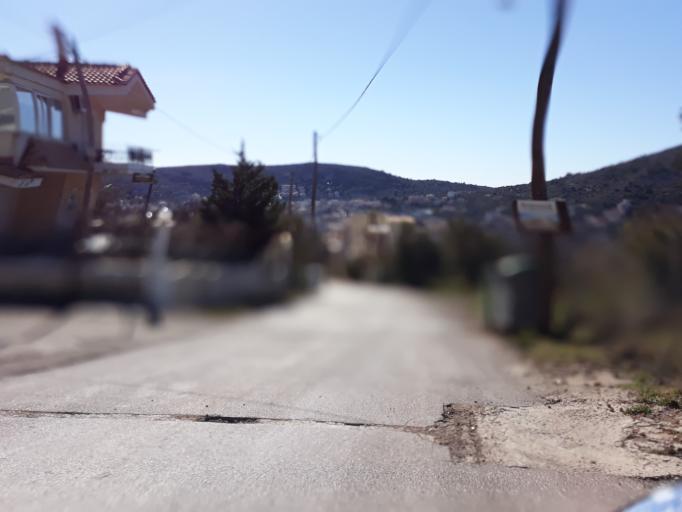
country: GR
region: Attica
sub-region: Nomarchia Dytikis Attikis
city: Fyli
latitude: 38.1121
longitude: 23.6739
